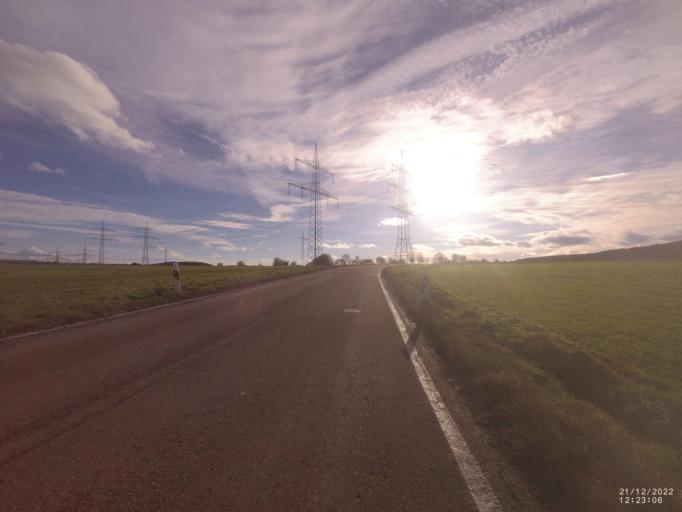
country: DE
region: Rheinland-Pfalz
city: Waldorf
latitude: 50.5069
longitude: 7.2321
